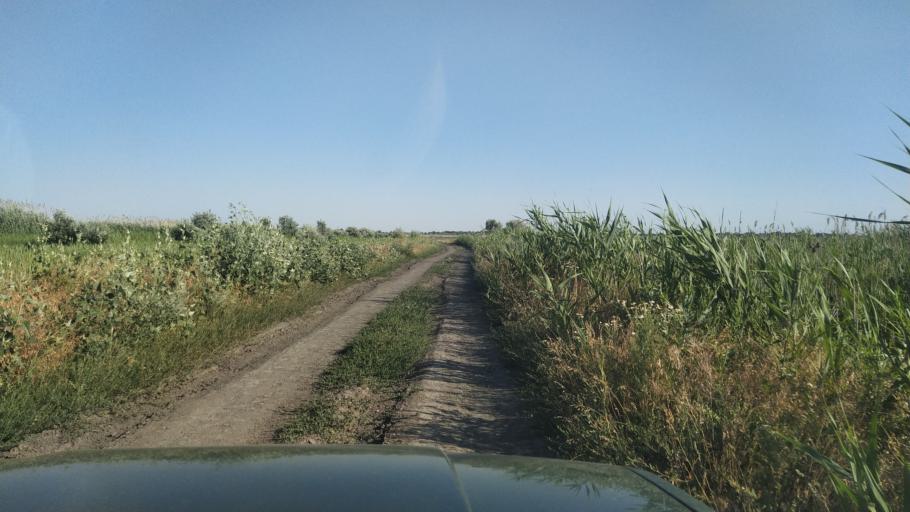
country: RU
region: Rostov
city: Kuleshovka
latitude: 47.1257
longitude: 39.6464
